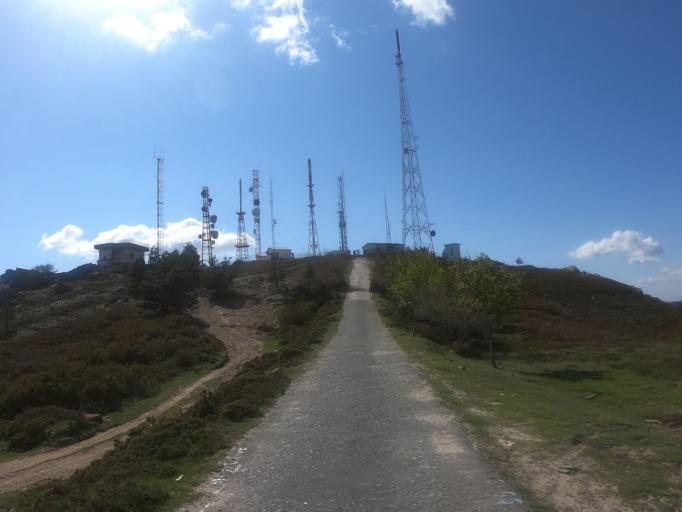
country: PT
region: Vila Real
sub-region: Mesao Frio
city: Mesao Frio
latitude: 41.2478
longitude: -7.8832
